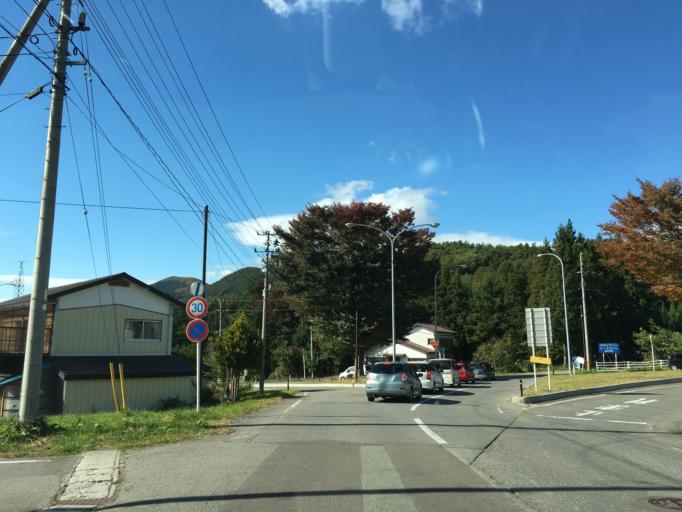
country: JP
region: Fukushima
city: Inawashiro
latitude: 37.6200
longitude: 140.2015
